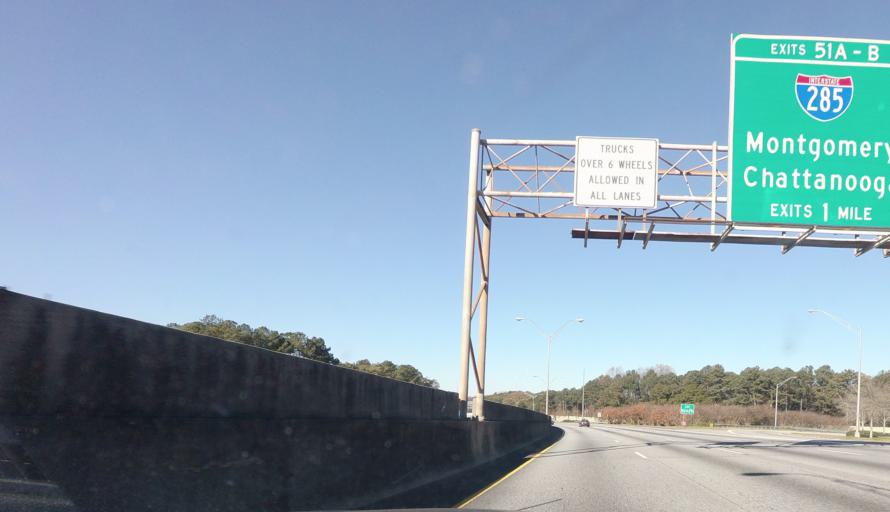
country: US
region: Georgia
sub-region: Fulton County
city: Atlanta
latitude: 33.7574
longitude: -84.4697
